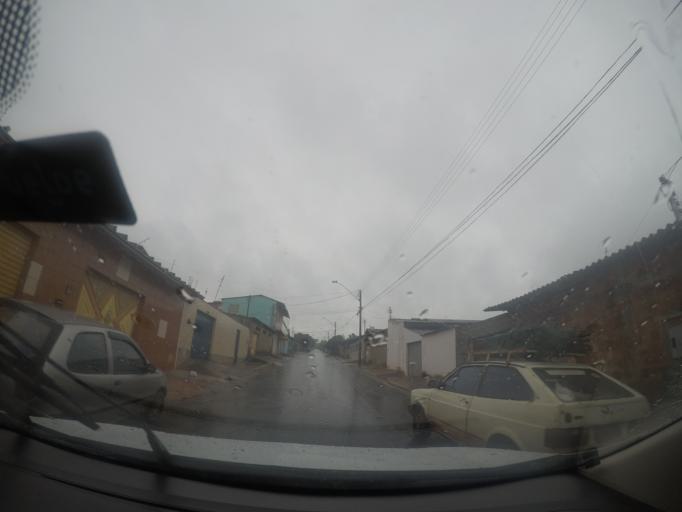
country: BR
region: Goias
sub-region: Goiania
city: Goiania
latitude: -16.5994
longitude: -49.3279
